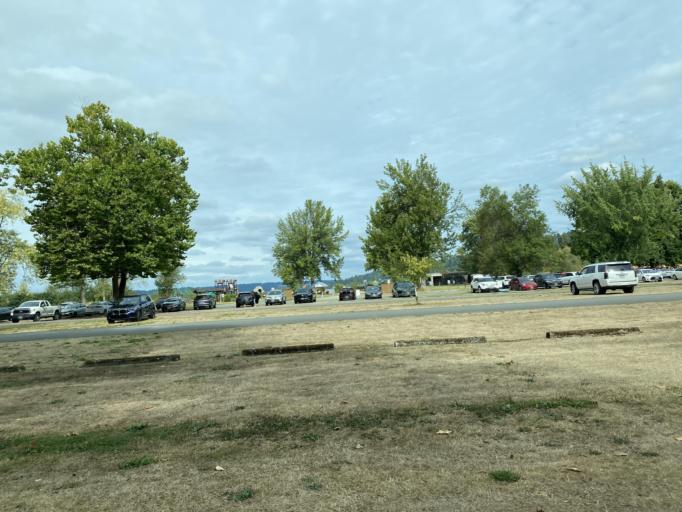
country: US
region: Washington
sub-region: King County
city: Issaquah
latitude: 47.5565
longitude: -122.0644
